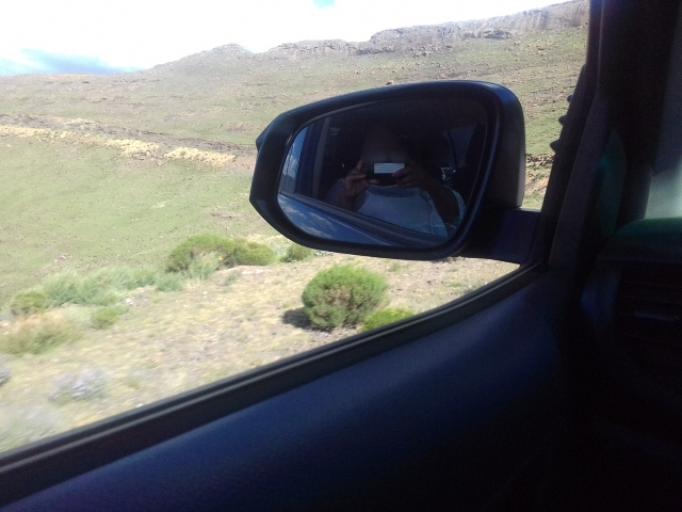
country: LS
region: Thaba-Tseka
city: Thaba-Tseka
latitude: -29.5248
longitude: 28.3437
